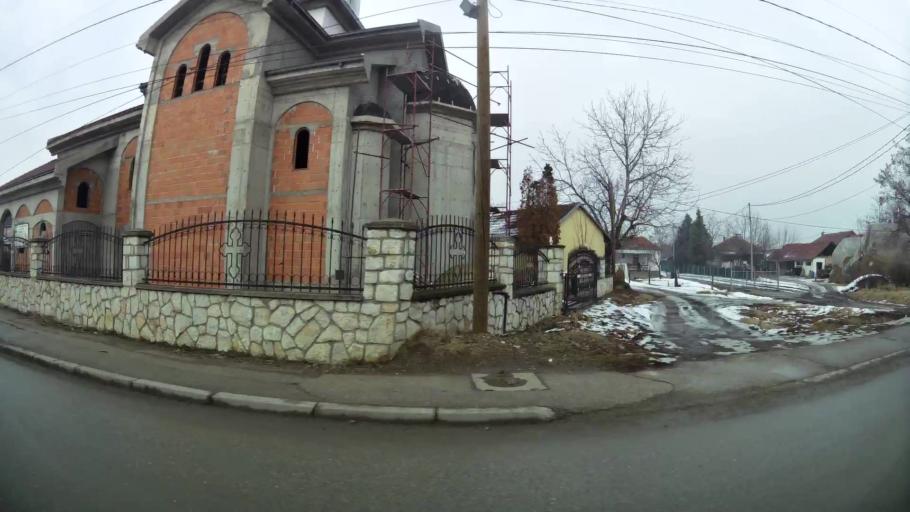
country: MK
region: Ilinden
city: Ilinden
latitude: 41.9946
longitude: 21.5768
